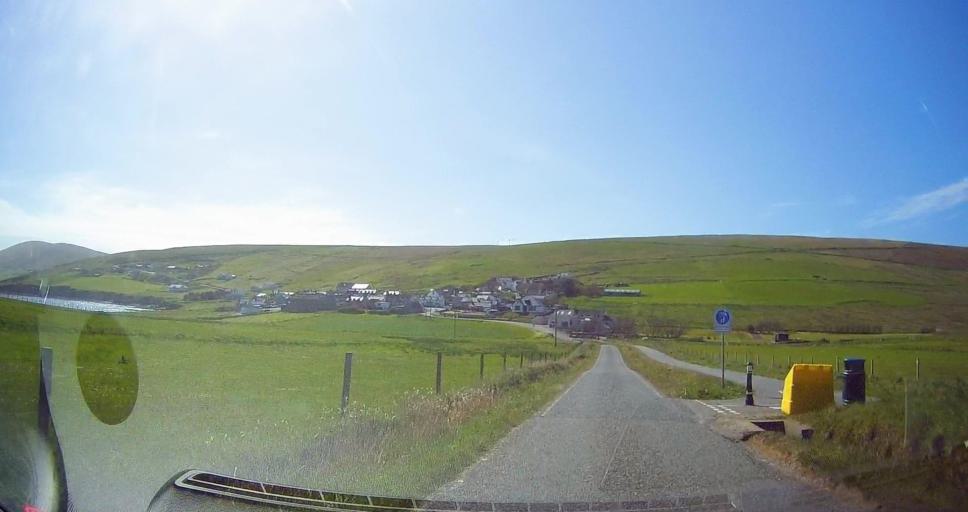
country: GB
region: Scotland
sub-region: Shetland Islands
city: Sandwick
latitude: 59.9990
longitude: -1.2495
